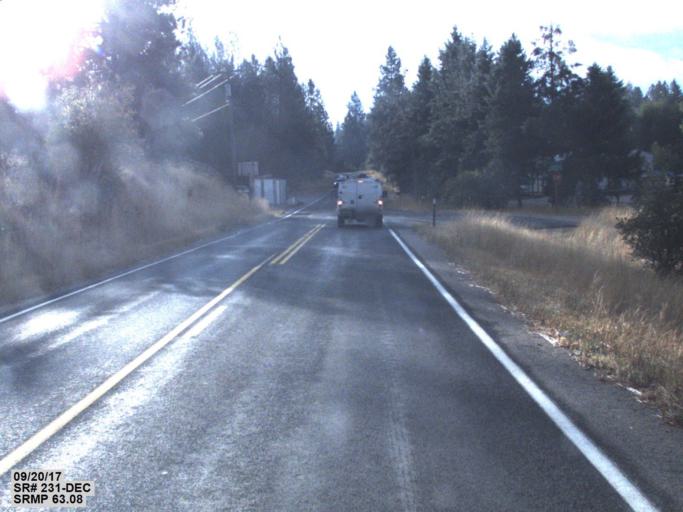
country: US
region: Washington
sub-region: Stevens County
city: Chewelah
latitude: 48.0599
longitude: -117.7571
